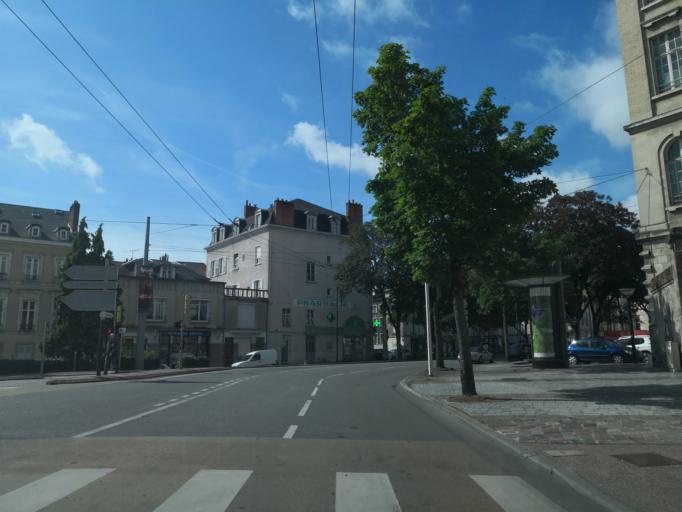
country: FR
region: Limousin
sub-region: Departement de la Haute-Vienne
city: Limoges
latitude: 45.8305
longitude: 1.2628
